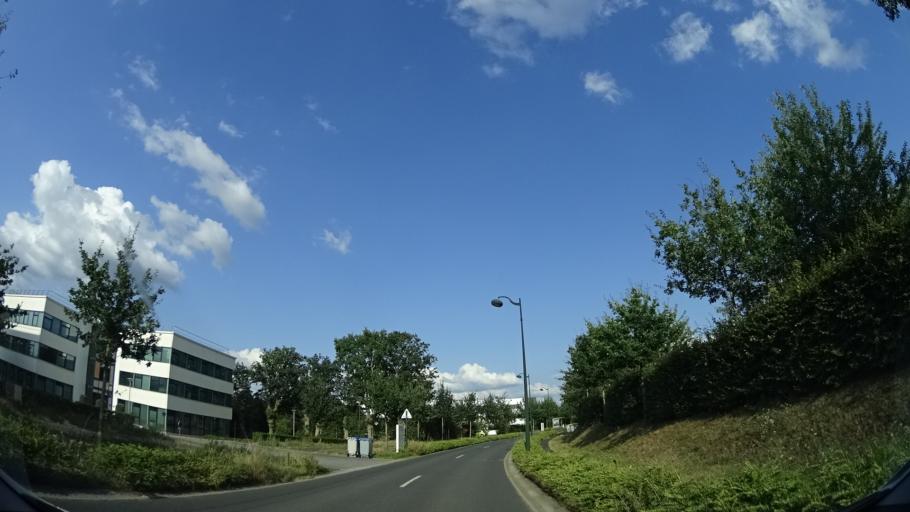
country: FR
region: Pays de la Loire
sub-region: Departement de la Loire-Atlantique
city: Carquefou
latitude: 47.3033
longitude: -1.5072
